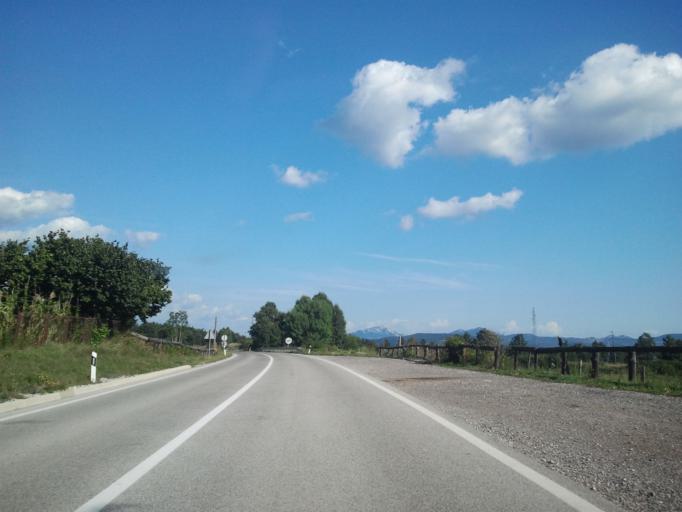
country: HR
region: Zadarska
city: Obrovac
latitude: 44.3796
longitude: 15.6453
